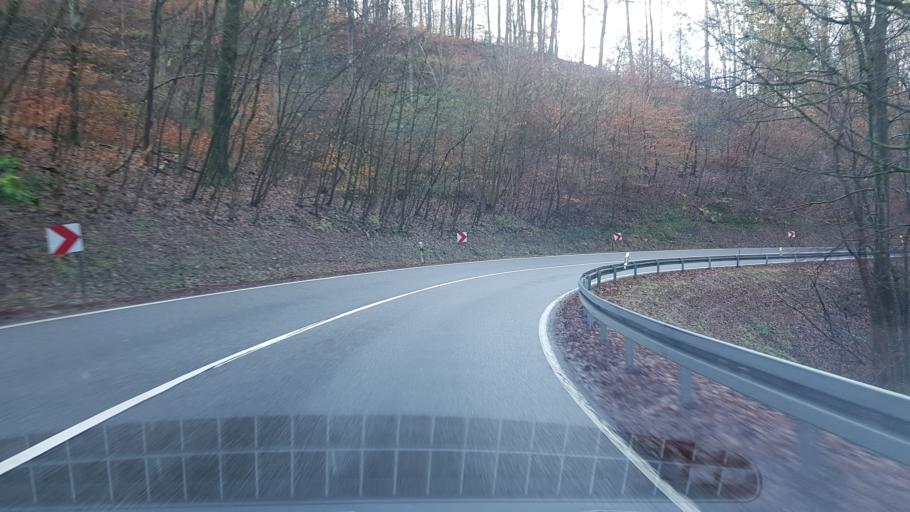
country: DE
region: Saarland
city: Sankt Ingbert
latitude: 49.2513
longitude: 7.1127
